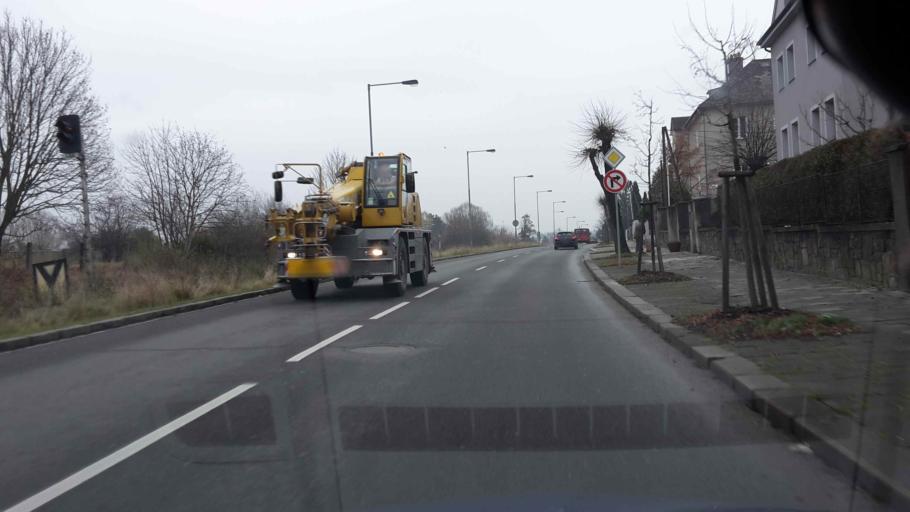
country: CZ
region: Olomoucky
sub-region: Okres Olomouc
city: Olomouc
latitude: 49.6039
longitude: 17.2343
